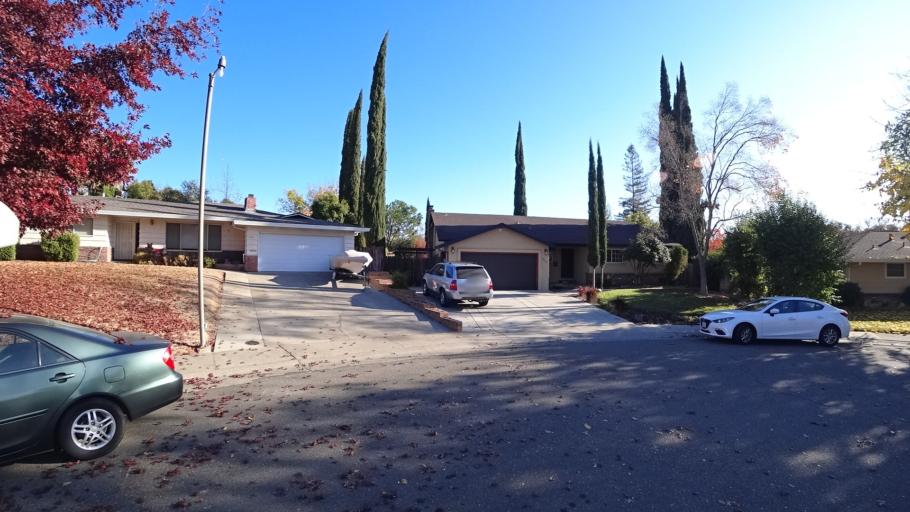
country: US
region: California
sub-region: Sacramento County
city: Fair Oaks
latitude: 38.6644
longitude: -121.2953
